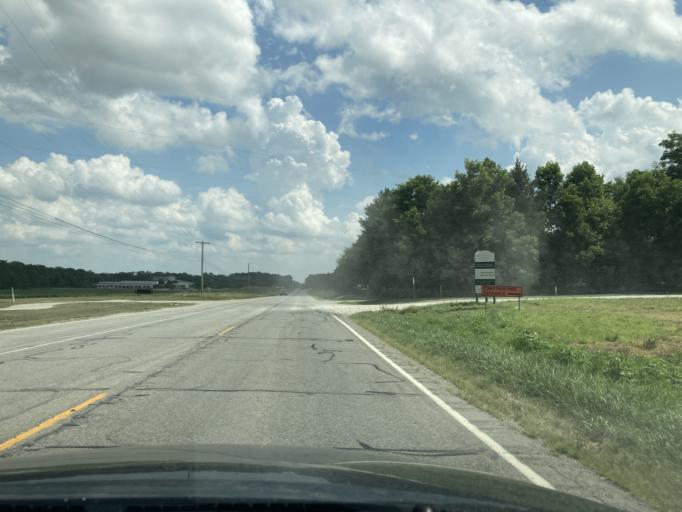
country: US
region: Indiana
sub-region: Boone County
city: Zionsville
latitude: 39.9908
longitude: -86.2610
